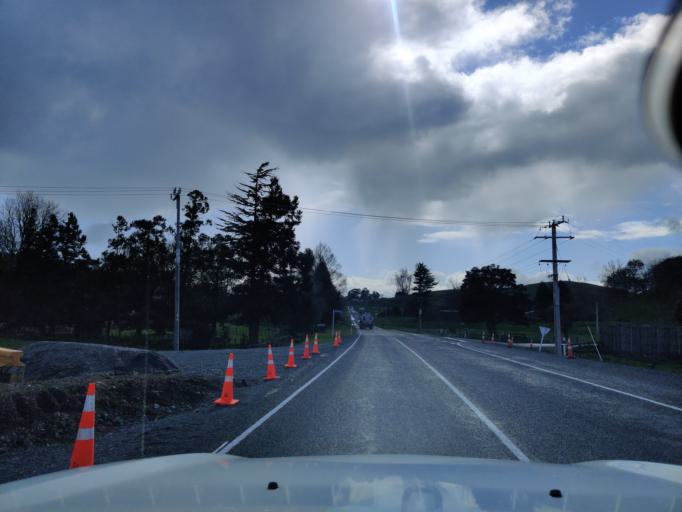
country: NZ
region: Waikato
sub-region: Waikato District
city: Ngaruawahia
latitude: -37.5949
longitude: 175.2068
